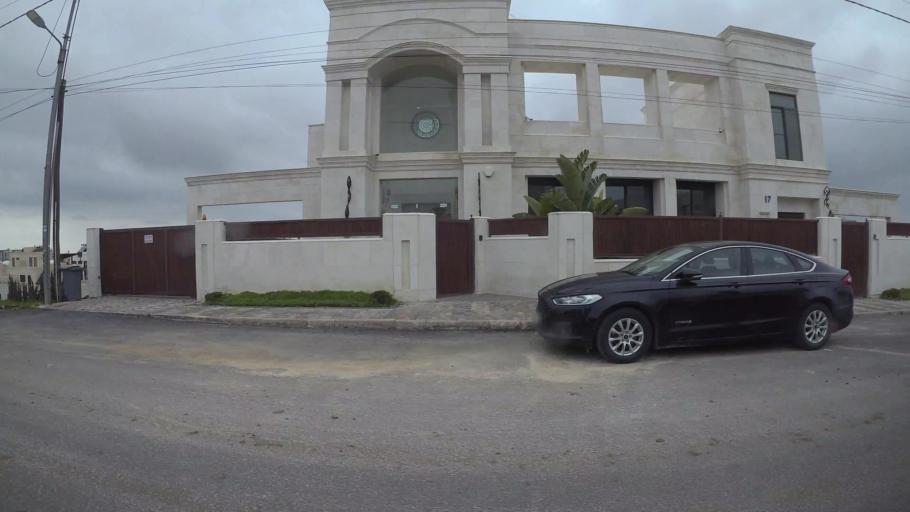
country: JO
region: Amman
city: Al Jubayhah
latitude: 31.9915
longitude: 35.8419
